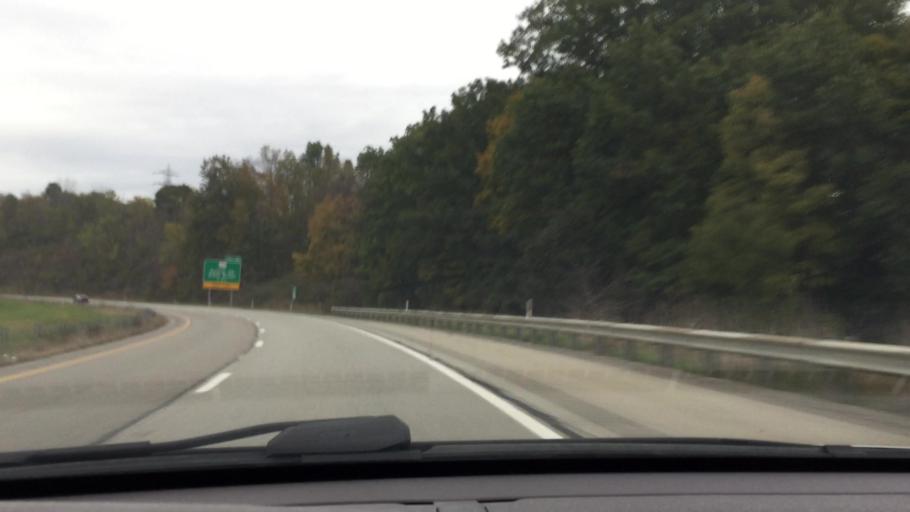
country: US
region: Pennsylvania
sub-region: Lawrence County
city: Oakland
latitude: 40.9930
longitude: -80.3882
